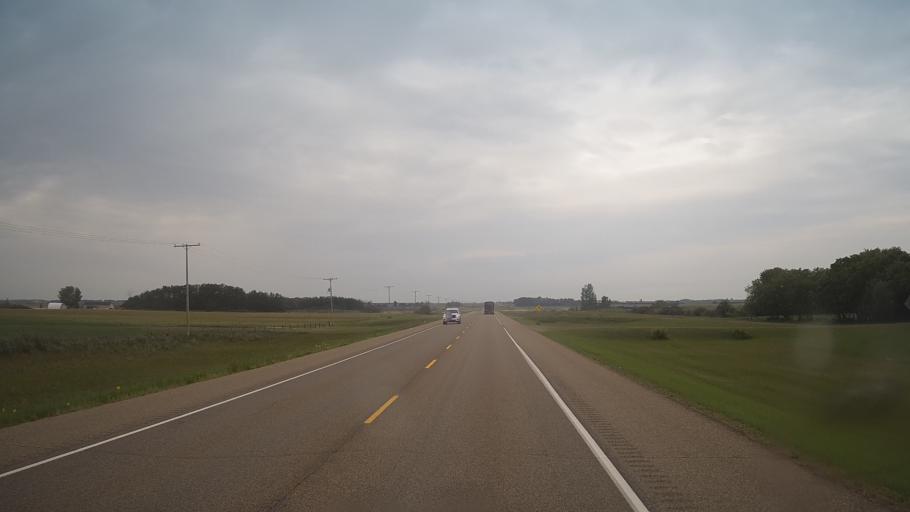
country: CA
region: Saskatchewan
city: Langham
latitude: 52.1289
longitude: -107.1198
